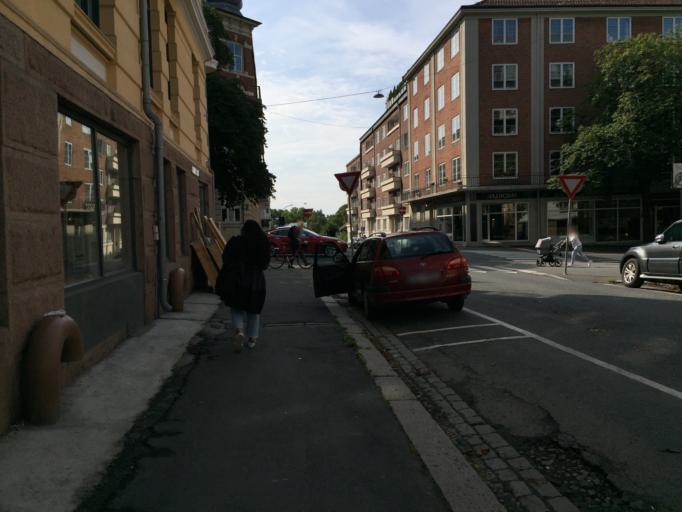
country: NO
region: Oslo
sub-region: Oslo
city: Sjolyststranda
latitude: 59.9195
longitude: 10.7018
